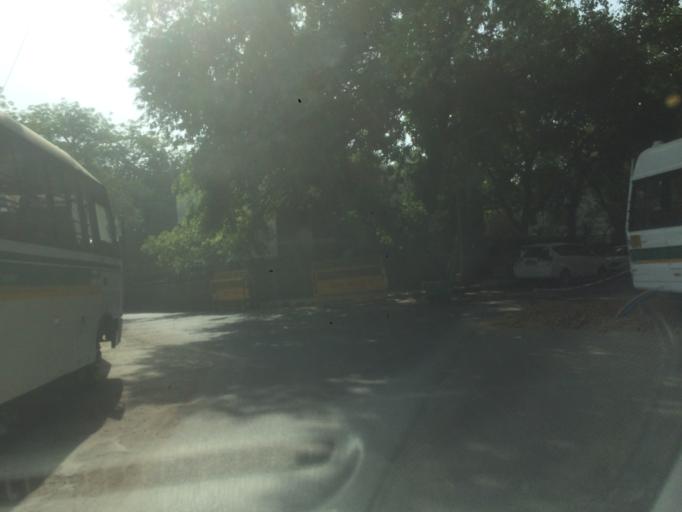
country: IN
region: NCT
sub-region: New Delhi
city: New Delhi
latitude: 28.6299
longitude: 77.2098
